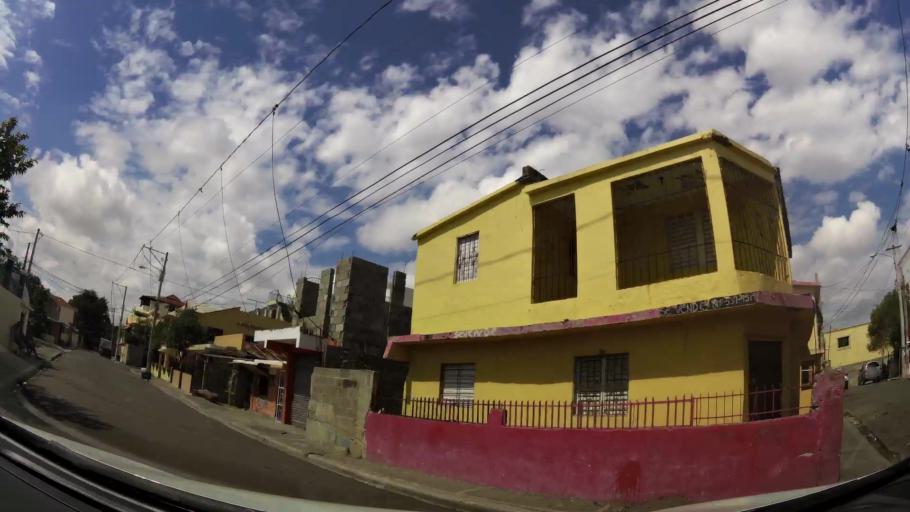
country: DO
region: Santiago
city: Santiago de los Caballeros
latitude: 19.4710
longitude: -70.6979
